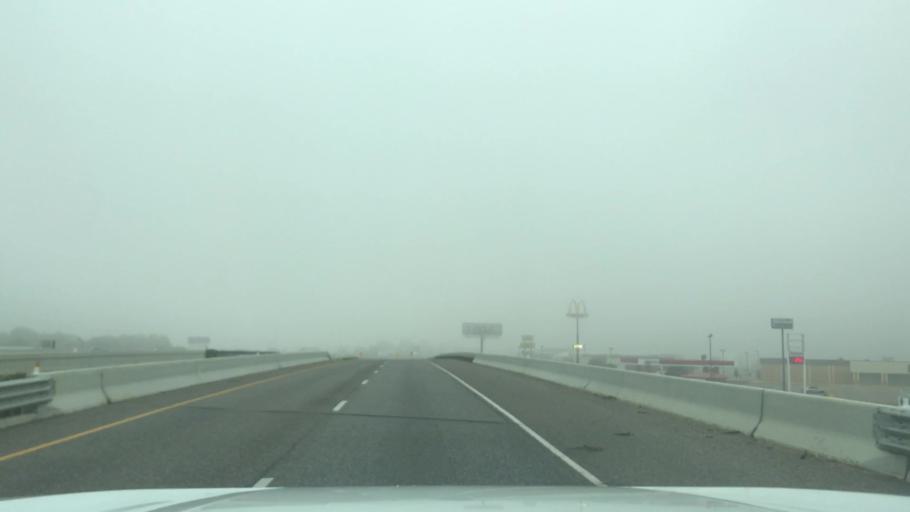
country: US
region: Texas
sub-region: Lubbock County
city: Slaton
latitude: 33.4343
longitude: -101.6644
